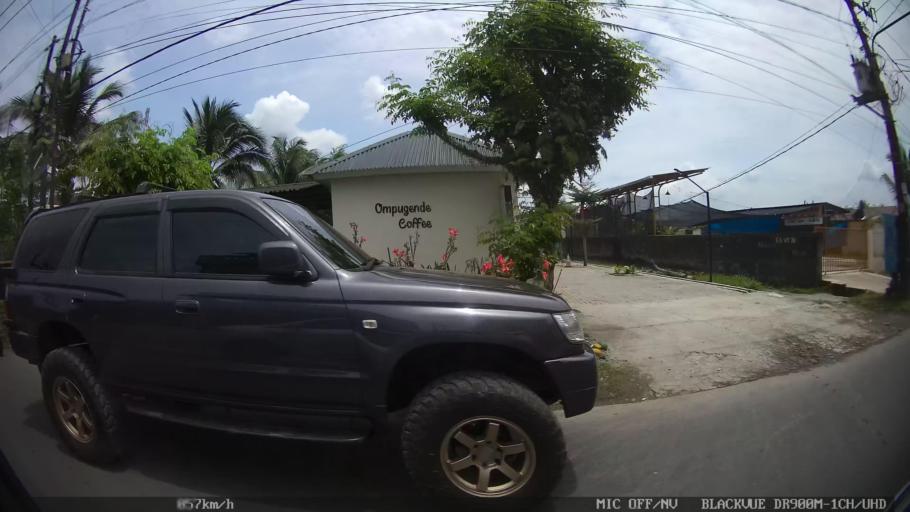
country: ID
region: North Sumatra
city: Sunggal
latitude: 3.5550
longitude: 98.6353
